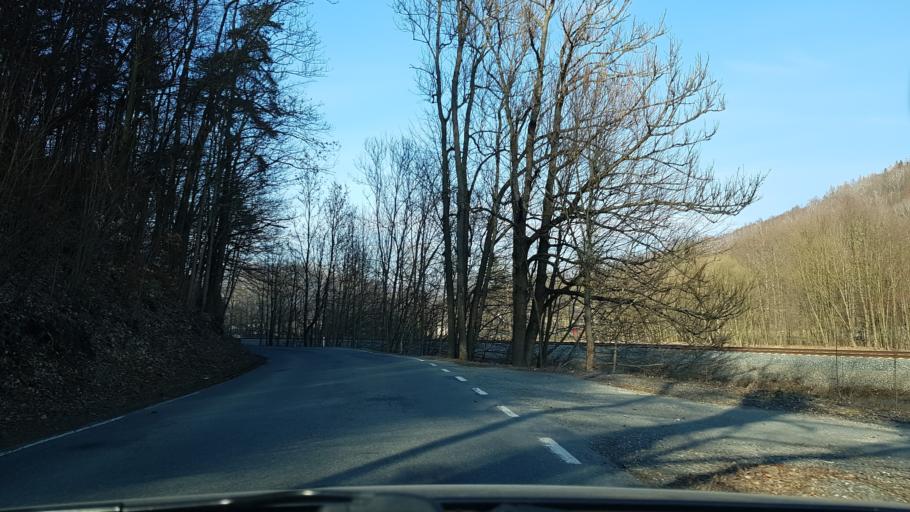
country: CZ
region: Olomoucky
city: Dolni Bohdikov
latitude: 50.0161
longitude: 16.8980
